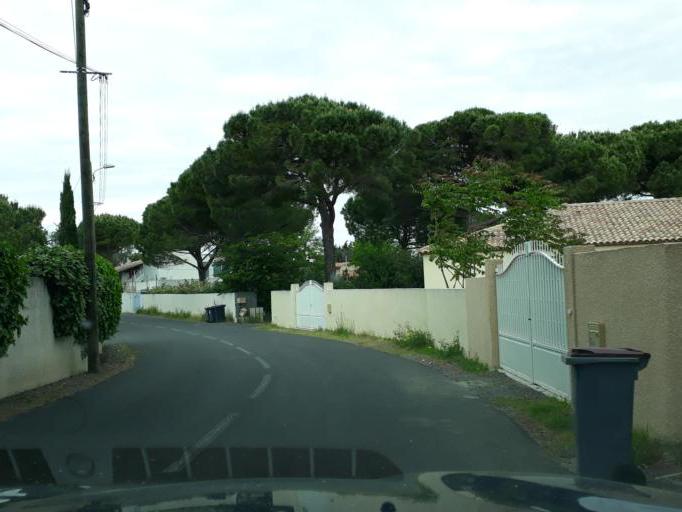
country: FR
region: Languedoc-Roussillon
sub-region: Departement de l'Herault
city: Agde
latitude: 43.2887
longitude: 3.4654
